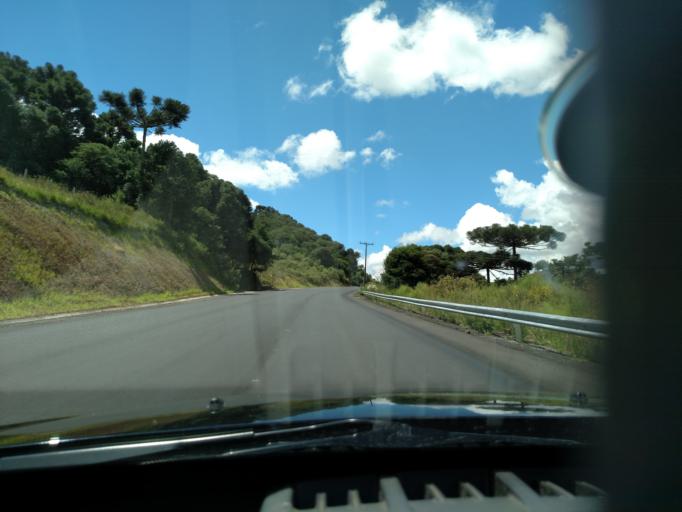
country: BR
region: Santa Catarina
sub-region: Sao Joaquim
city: Sao Joaquim
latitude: -28.2456
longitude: -49.9699
